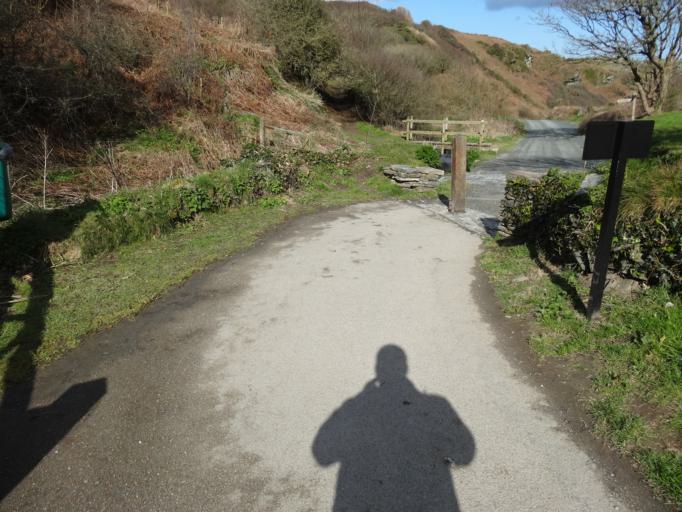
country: GB
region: England
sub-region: Cornwall
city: Tintagel
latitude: 50.6646
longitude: -4.7554
